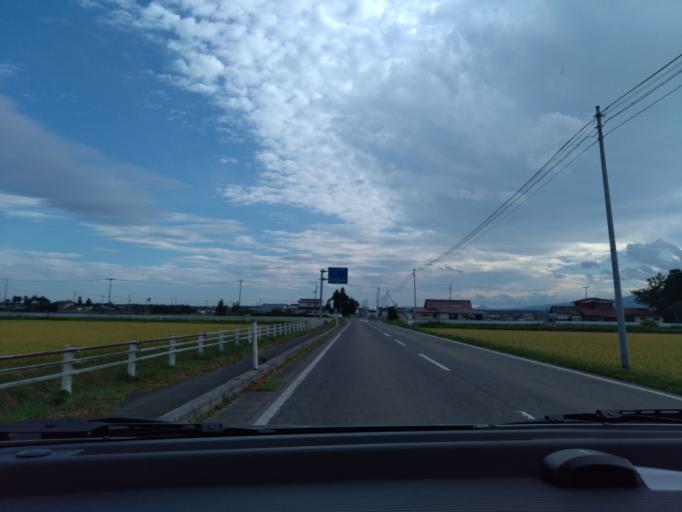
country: JP
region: Iwate
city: Kitakami
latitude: 39.3039
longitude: 141.0509
